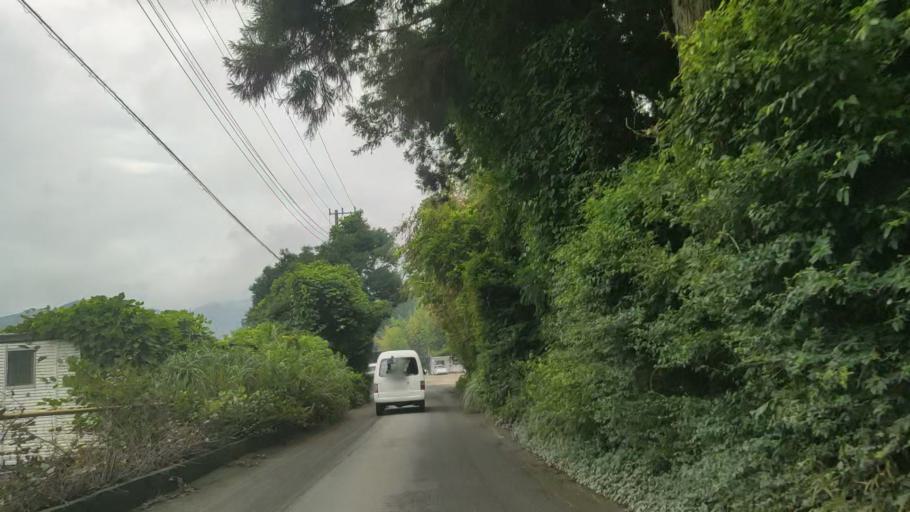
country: JP
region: Shizuoka
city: Fujinomiya
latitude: 35.2163
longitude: 138.5441
